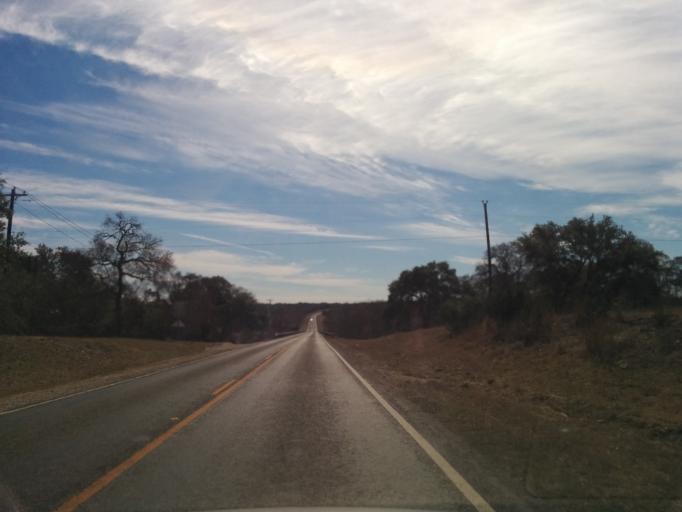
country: US
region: Texas
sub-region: Bexar County
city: Fair Oaks Ranch
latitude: 29.8942
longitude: -98.5599
